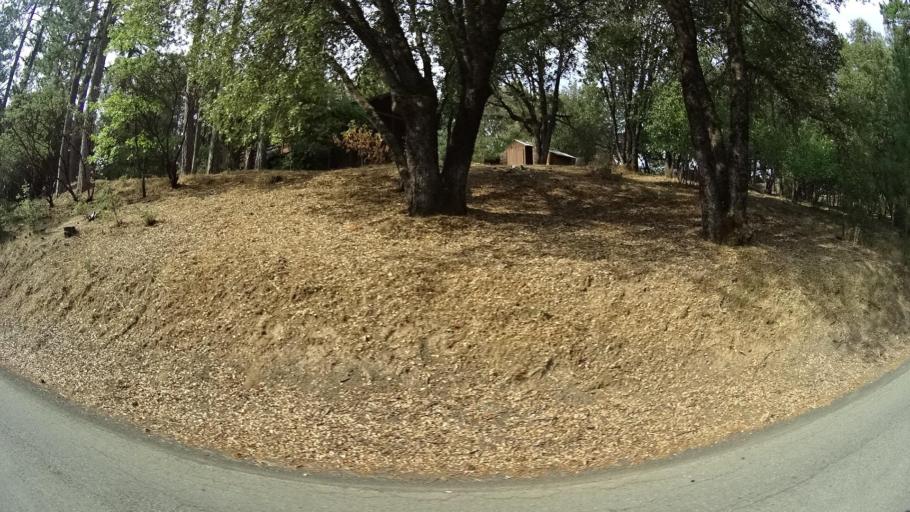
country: US
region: California
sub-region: Mariposa County
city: Midpines
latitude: 37.5065
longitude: -119.8214
